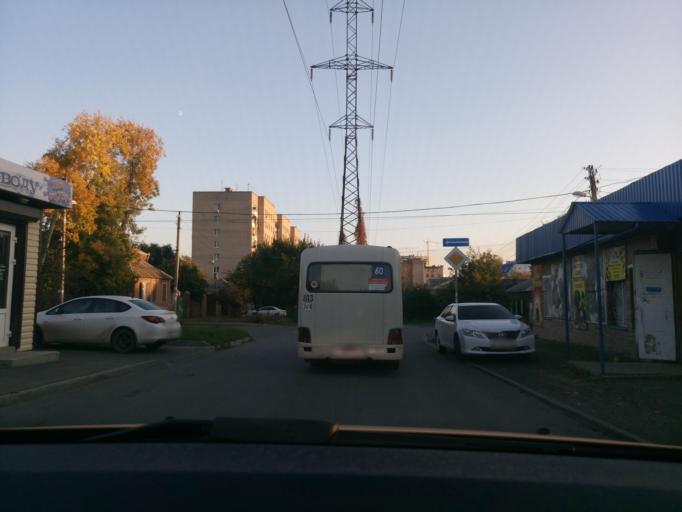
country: RU
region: Rostov
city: Rostov-na-Donu
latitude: 47.2334
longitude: 39.6885
